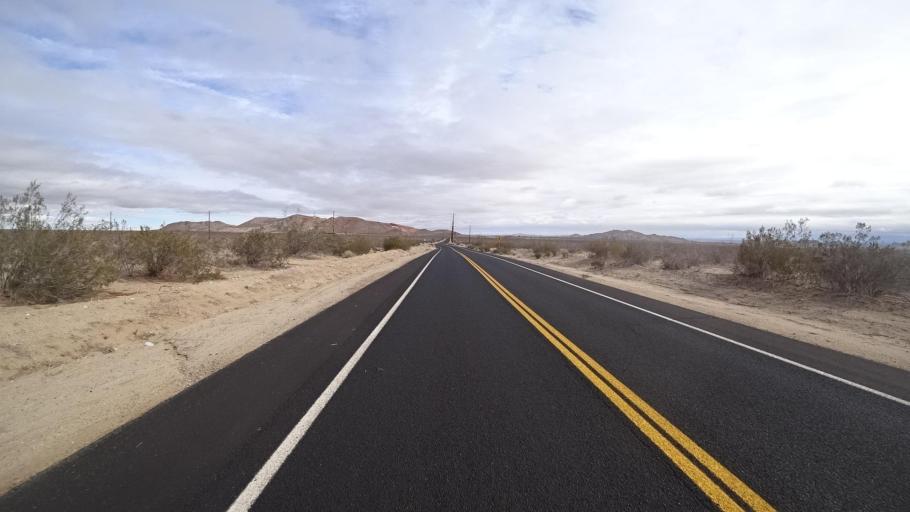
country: US
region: California
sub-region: Kern County
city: Mojave
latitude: 34.9509
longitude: -118.3118
